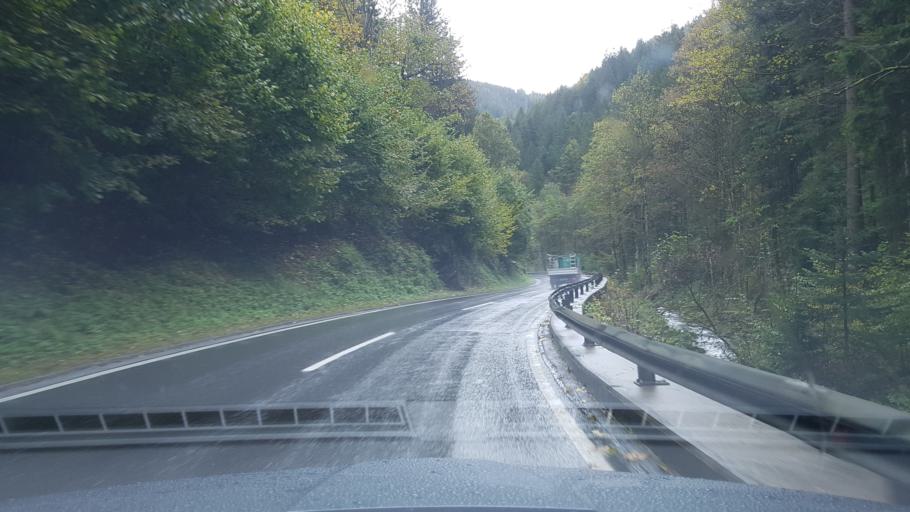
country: AT
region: Styria
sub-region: Politischer Bezirk Voitsberg
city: Salla
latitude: 47.1127
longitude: 15.0011
